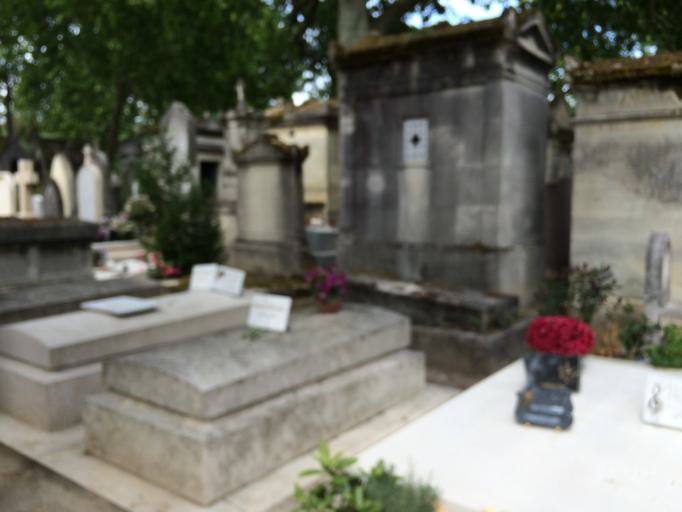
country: FR
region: Ile-de-France
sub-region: Departement de Seine-Saint-Denis
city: Bagnolet
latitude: 48.8611
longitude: 2.3950
